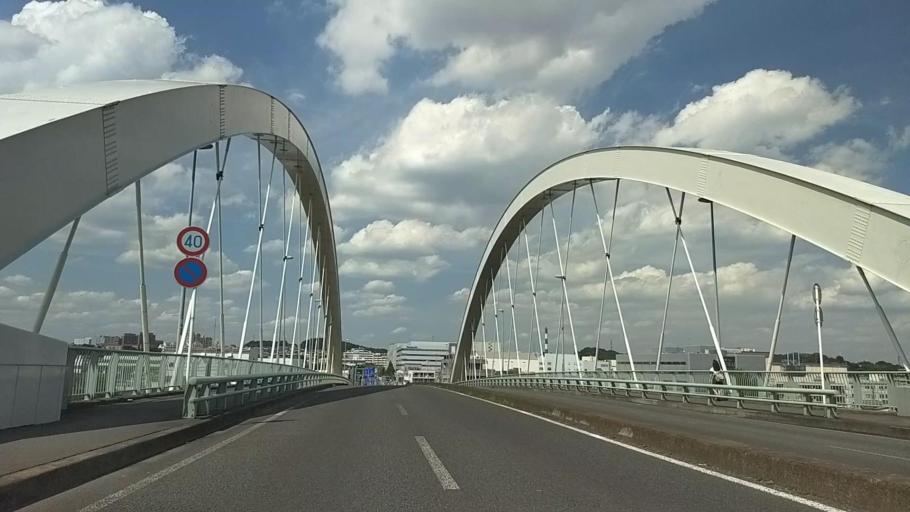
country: JP
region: Kanagawa
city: Yokohama
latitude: 35.5114
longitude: 139.5645
